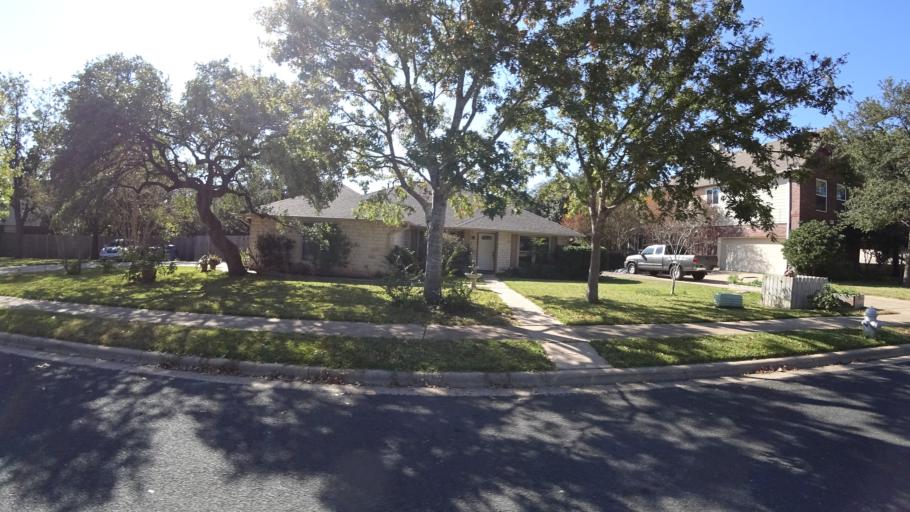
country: US
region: Texas
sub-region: Travis County
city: Shady Hollow
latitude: 30.2201
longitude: -97.8658
